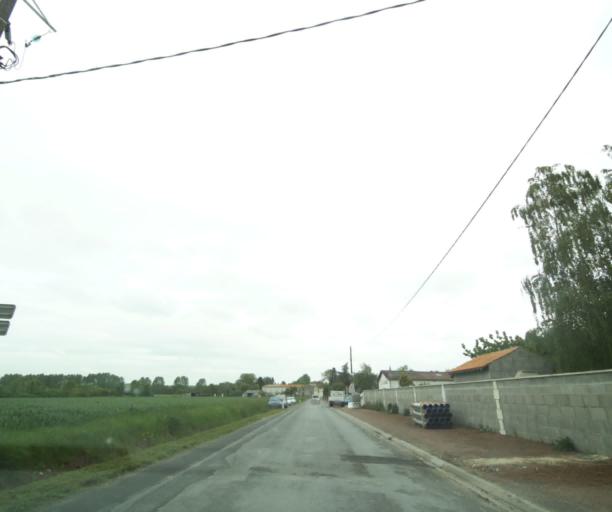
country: FR
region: Poitou-Charentes
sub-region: Departement de la Charente-Maritime
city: Chaniers
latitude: 45.6982
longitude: -0.5282
